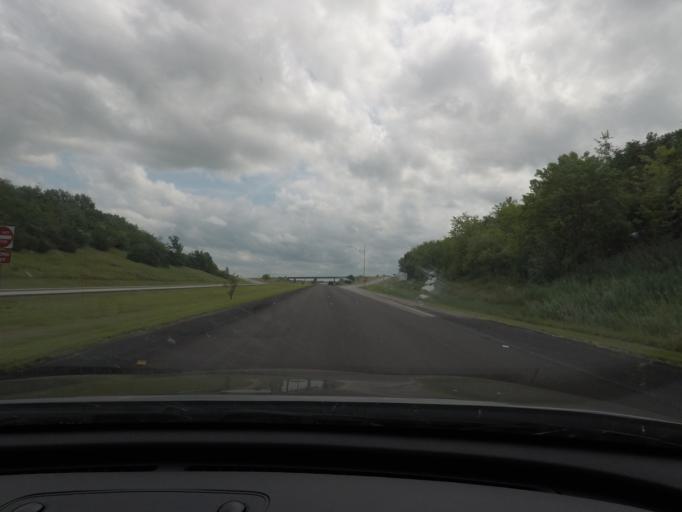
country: US
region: Missouri
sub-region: Carroll County
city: Carrollton
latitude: 39.3635
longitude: -93.4836
